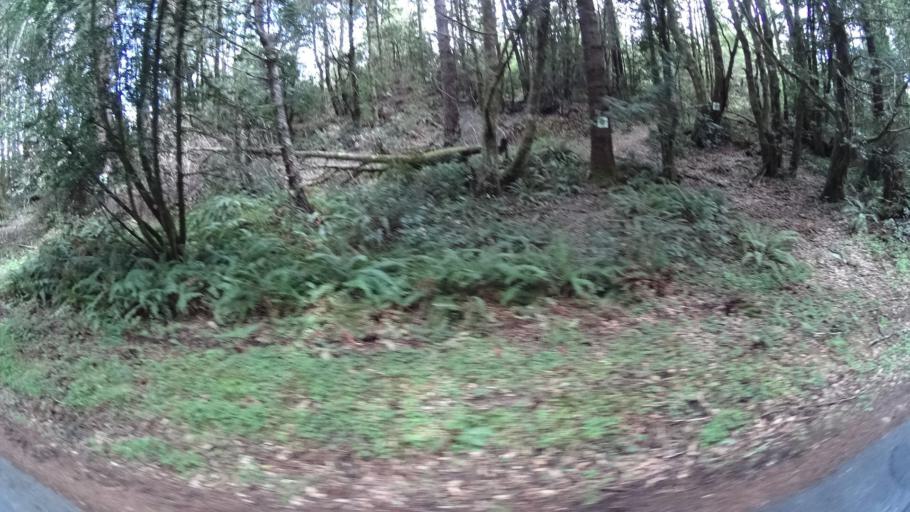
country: US
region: California
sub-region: Humboldt County
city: Blue Lake
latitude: 40.7964
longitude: -123.9812
